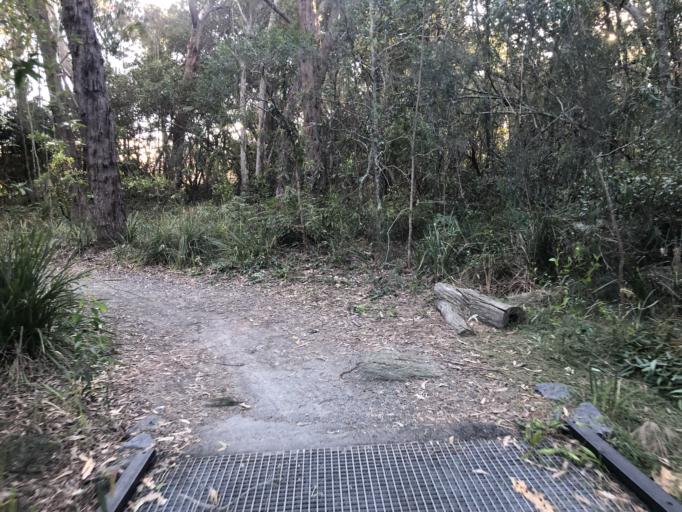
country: AU
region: New South Wales
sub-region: Coffs Harbour
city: Coffs Harbour
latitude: -30.2883
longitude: 153.1271
